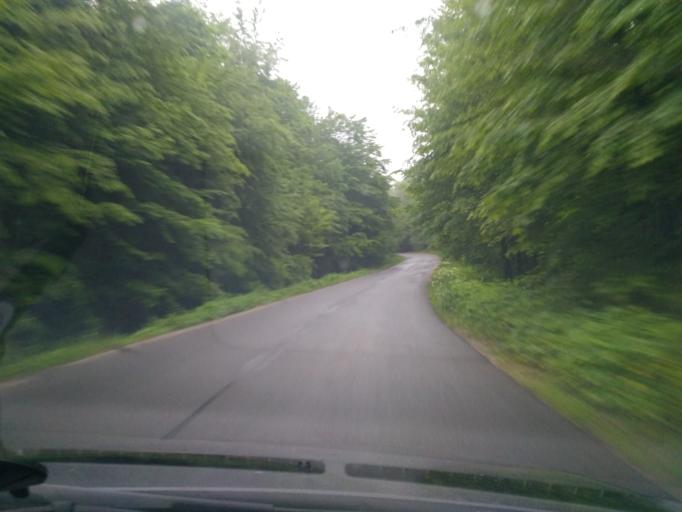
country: PL
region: Subcarpathian Voivodeship
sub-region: Powiat debicki
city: Debica
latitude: 49.9734
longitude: 21.3862
